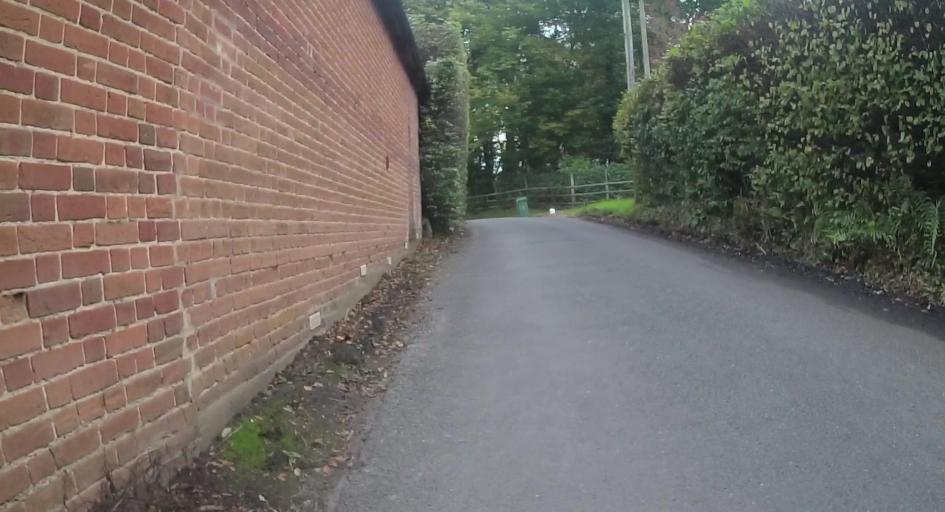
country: GB
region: England
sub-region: Hampshire
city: Hook
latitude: 51.2999
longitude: -0.9270
